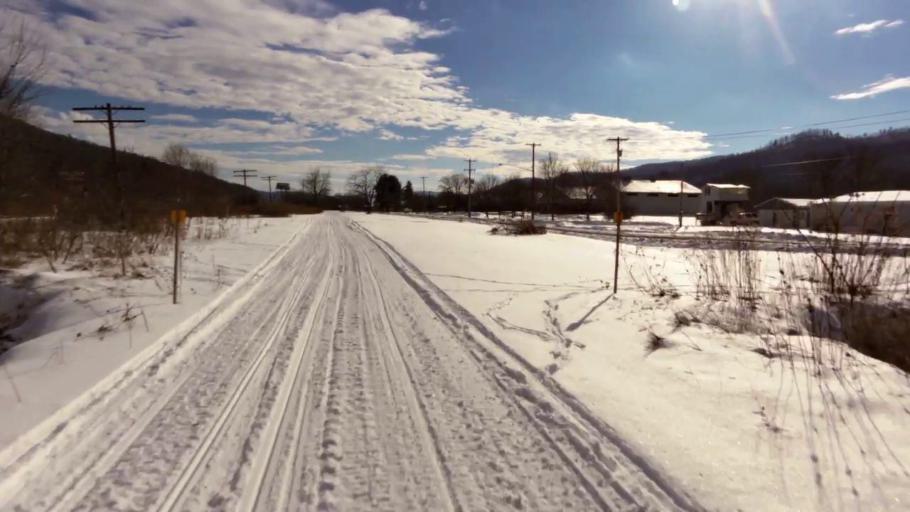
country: US
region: Pennsylvania
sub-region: McKean County
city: Foster Brook
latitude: 42.0264
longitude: -78.6314
